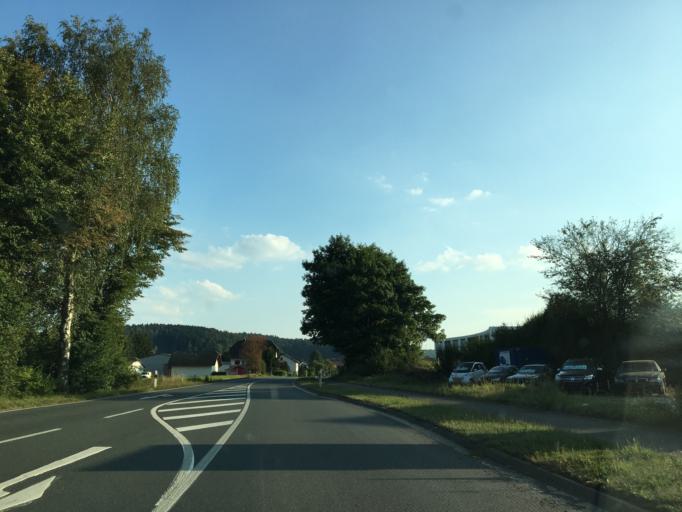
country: DE
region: Hesse
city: Frankenberg
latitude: 51.0353
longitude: 8.8115
